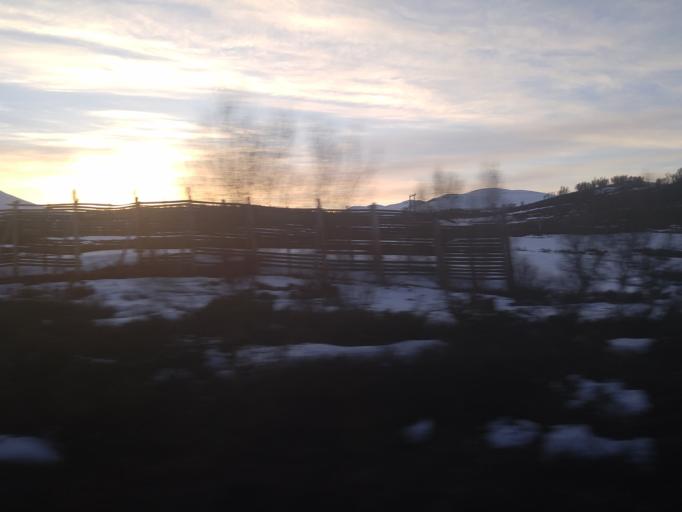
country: NO
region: Sor-Trondelag
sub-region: Oppdal
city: Oppdal
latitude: 62.2819
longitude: 9.5918
